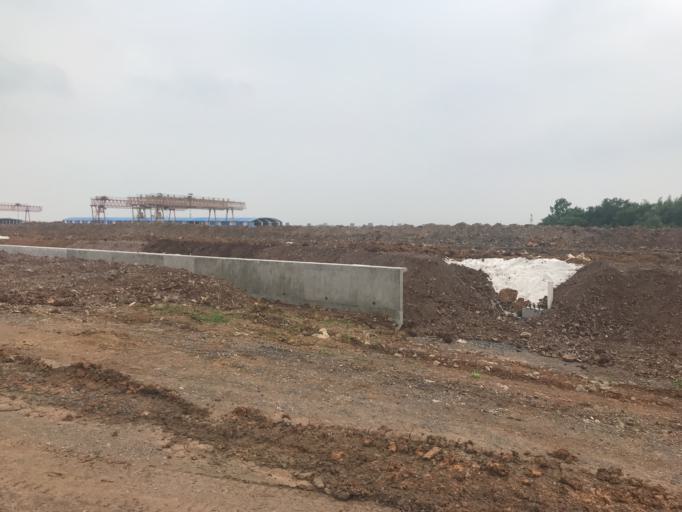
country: CN
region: Hubei
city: Anlu
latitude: 31.2580
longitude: 113.6462
